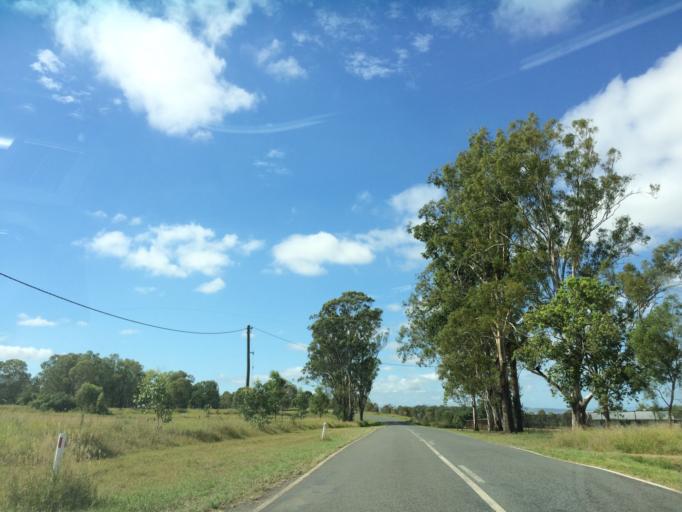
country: AU
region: Queensland
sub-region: Logan
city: Cedar Vale
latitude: -27.8865
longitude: 152.9725
